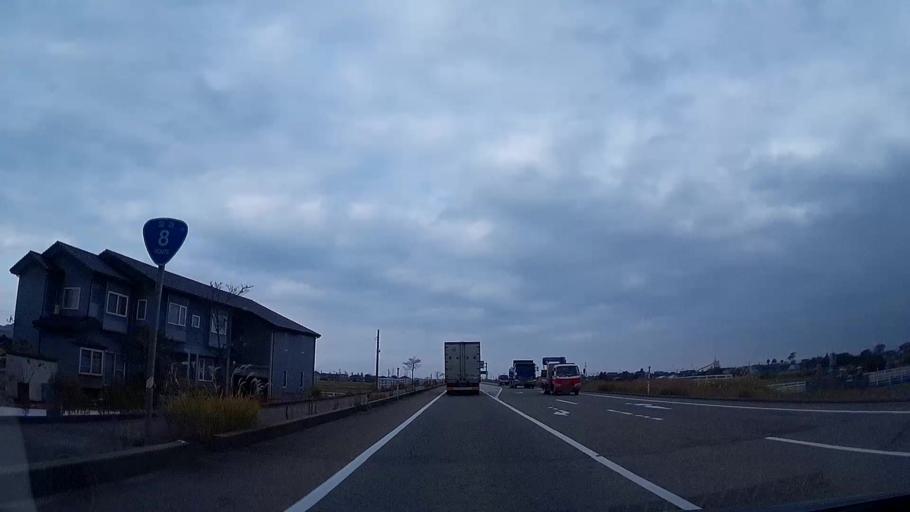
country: JP
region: Toyama
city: Nyuzen
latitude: 36.8932
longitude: 137.4446
